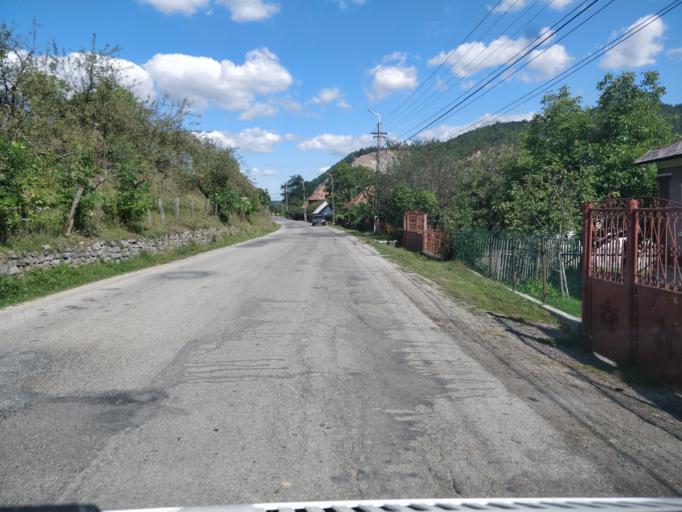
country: RO
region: Cluj
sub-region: Comuna Poeni
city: Poeni
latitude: 46.8886
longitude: 22.8755
